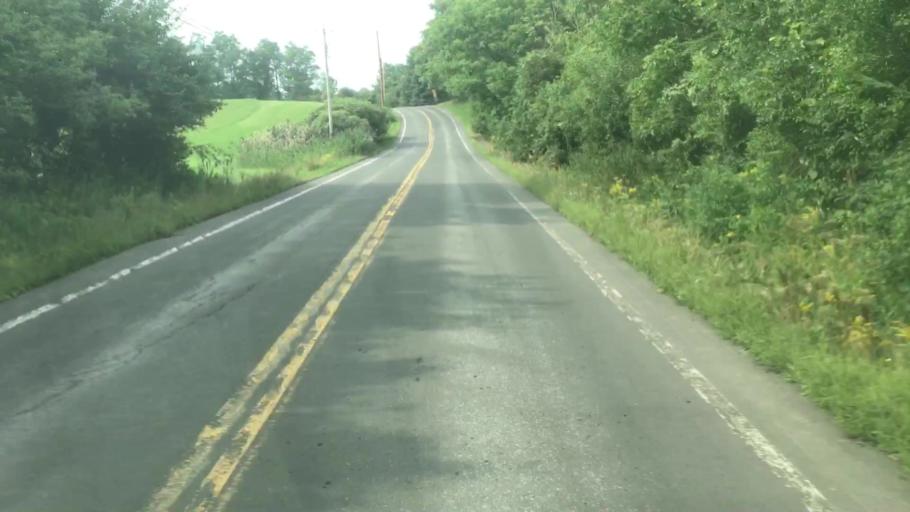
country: US
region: New York
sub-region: Onondaga County
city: Skaneateles
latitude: 42.9048
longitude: -76.4517
